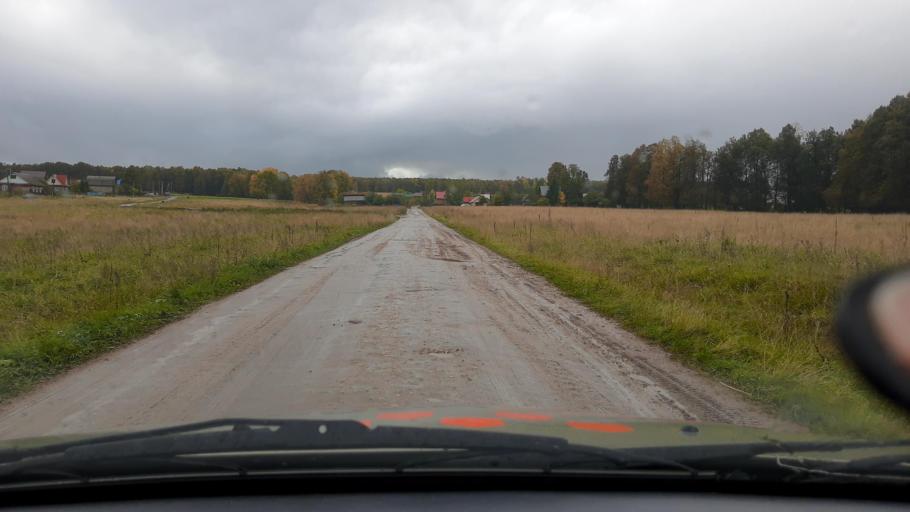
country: RU
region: Bashkortostan
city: Kudeyevskiy
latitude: 54.8781
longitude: 56.6297
